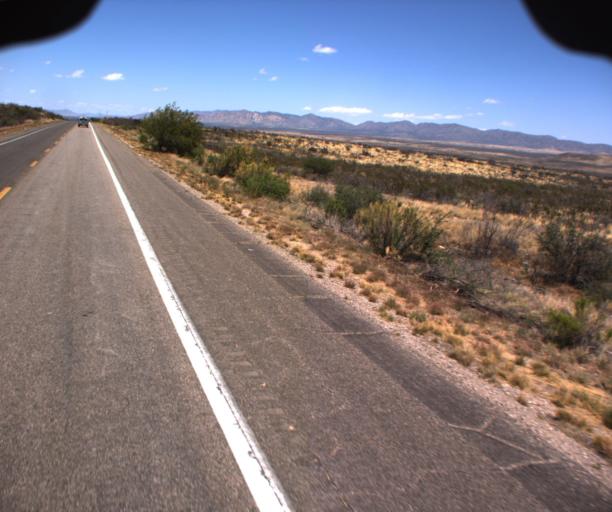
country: US
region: Arizona
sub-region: Cochise County
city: Tombstone
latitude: 31.6780
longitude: -110.0327
